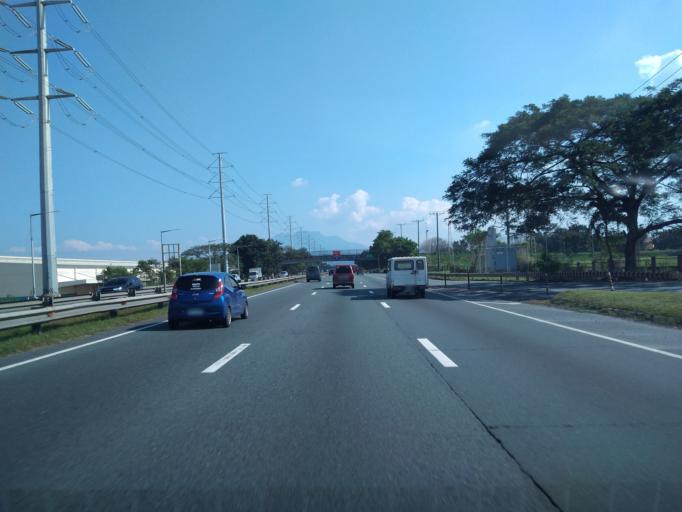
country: PH
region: Calabarzon
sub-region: Province of Laguna
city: Cabuyao
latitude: 14.2347
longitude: 121.1163
